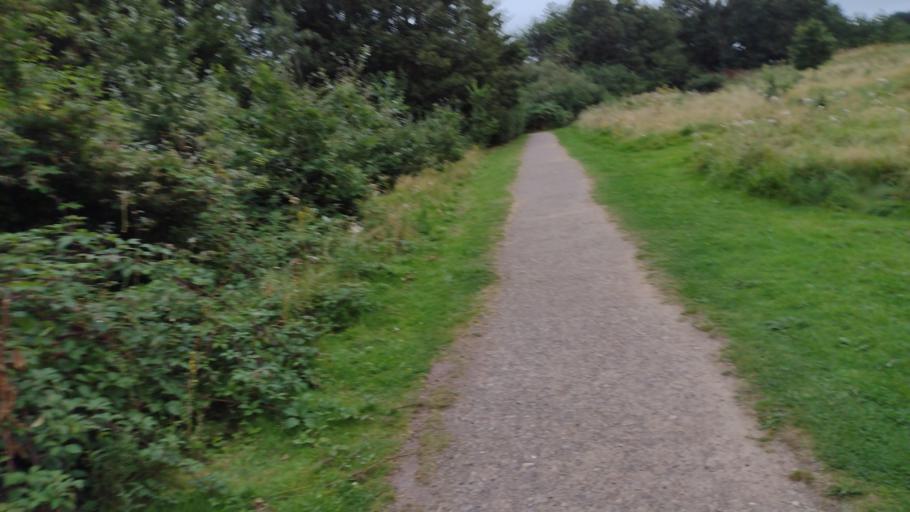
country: GB
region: England
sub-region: Wokingham
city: Winnersh
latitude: 51.4374
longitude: -0.8782
